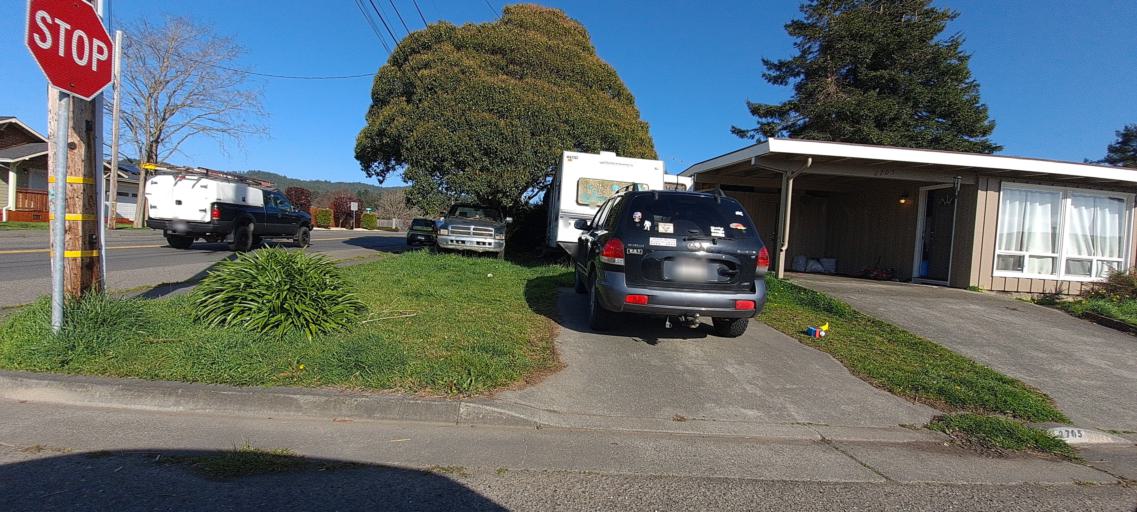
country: US
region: California
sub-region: Humboldt County
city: Fortuna
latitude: 40.5774
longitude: -124.1371
